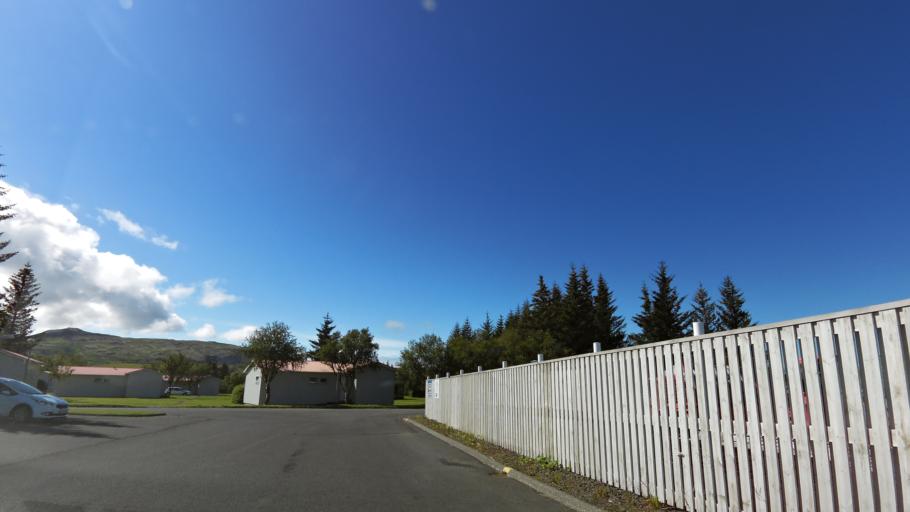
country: IS
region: Capital Region
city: Mosfellsbaer
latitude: 64.1645
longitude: -21.6643
